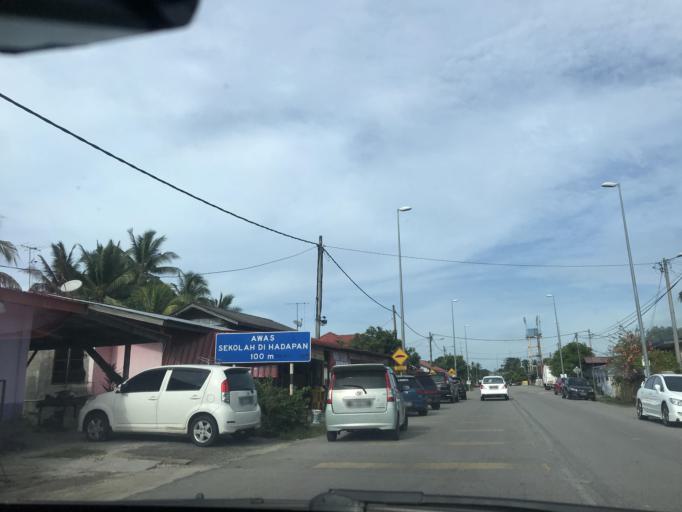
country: MY
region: Kelantan
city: Kota Bharu
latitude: 6.1380
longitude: 102.2133
